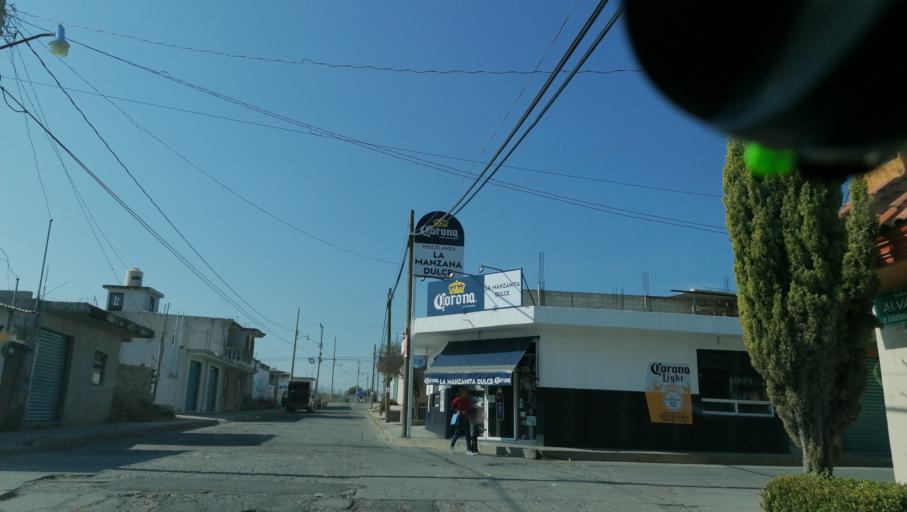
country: MX
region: Puebla
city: Domingo Arenas
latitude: 19.1401
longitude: -98.4540
